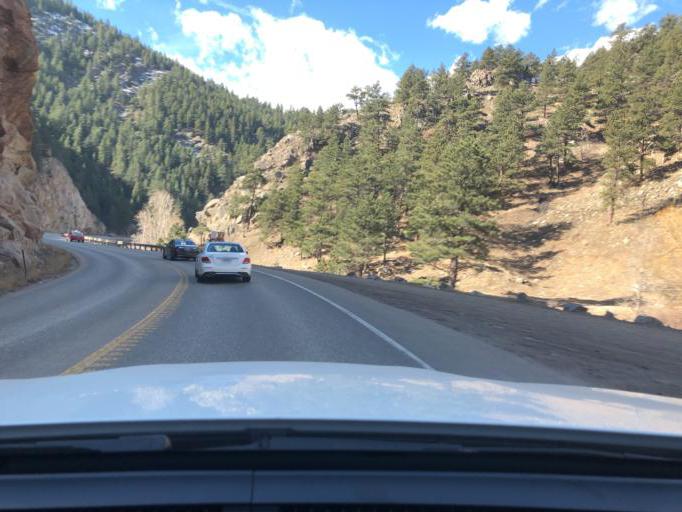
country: US
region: Colorado
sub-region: Boulder County
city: Boulder
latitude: 40.0149
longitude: -105.3139
